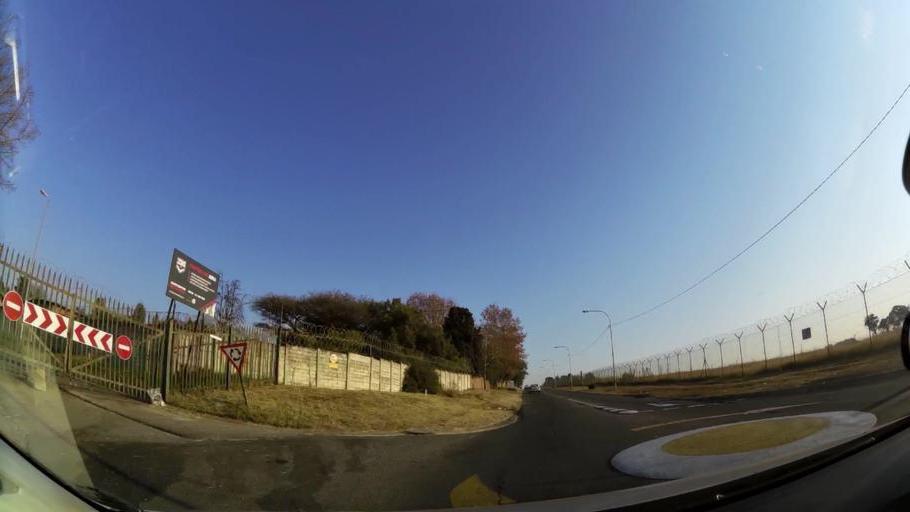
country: ZA
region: Gauteng
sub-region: City of Johannesburg Metropolitan Municipality
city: Modderfontein
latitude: -26.0802
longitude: 28.1041
